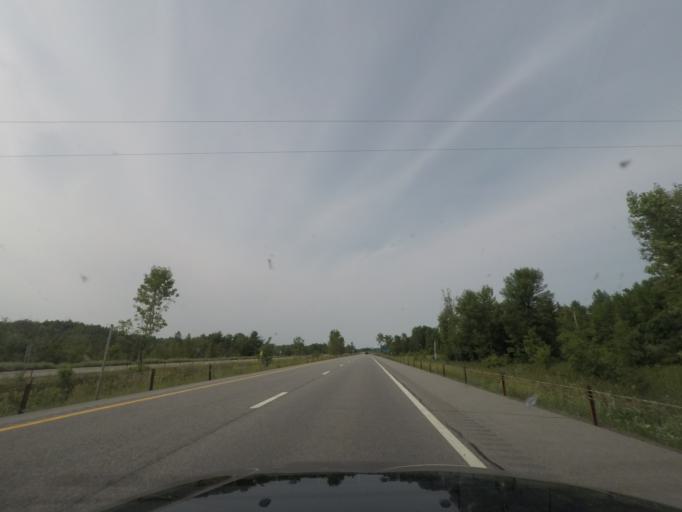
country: US
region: New York
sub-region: Essex County
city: Keeseville
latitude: 44.4350
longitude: -73.4916
